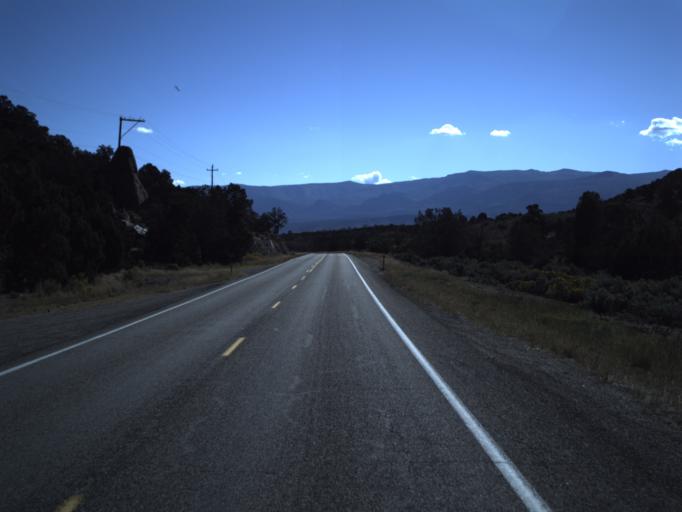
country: US
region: Utah
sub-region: Iron County
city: Cedar City
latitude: 37.6362
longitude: -113.2768
